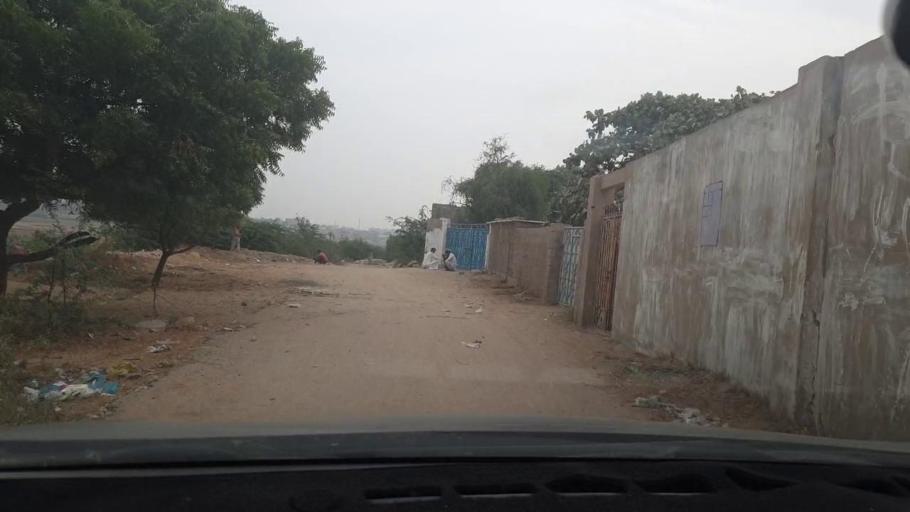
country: PK
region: Sindh
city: Malir Cantonment
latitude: 24.8690
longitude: 67.2527
